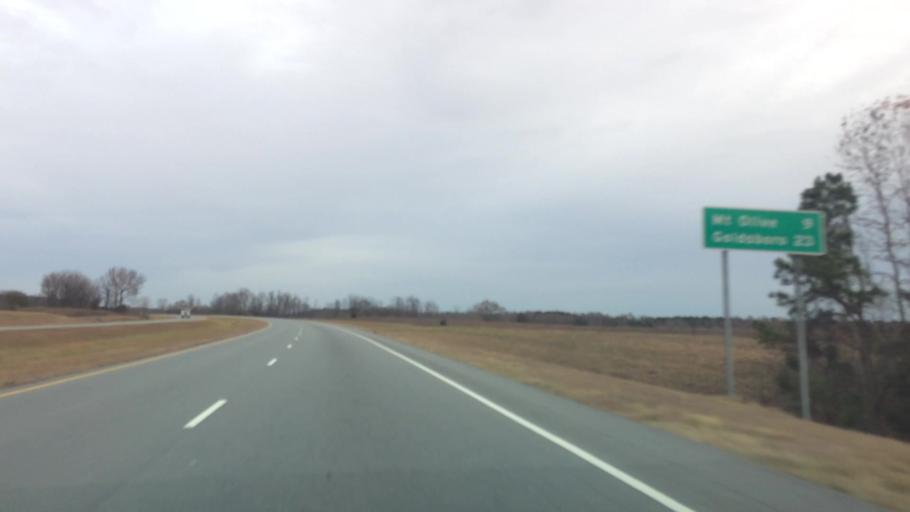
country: US
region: North Carolina
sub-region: Wayne County
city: Mount Olive
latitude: 35.1281
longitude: -78.1509
